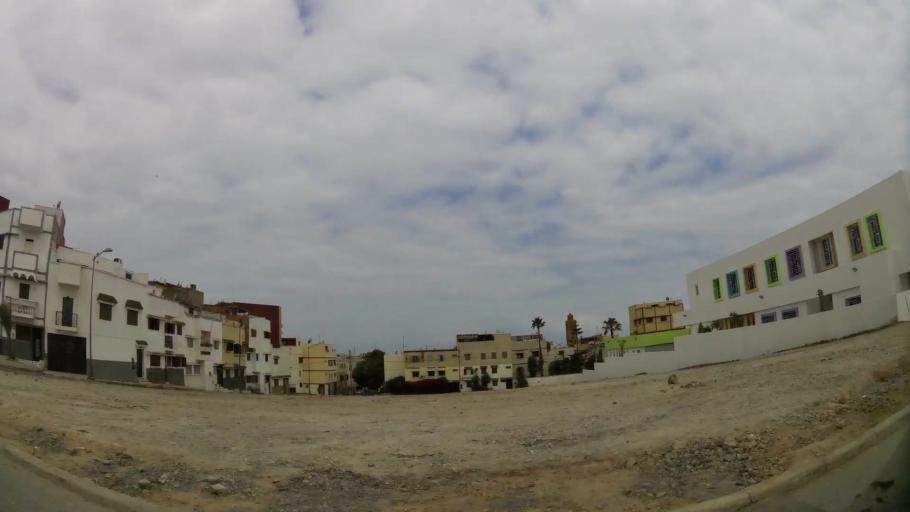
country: MA
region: Rabat-Sale-Zemmour-Zaer
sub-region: Rabat
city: Rabat
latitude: 33.9965
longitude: -6.8722
